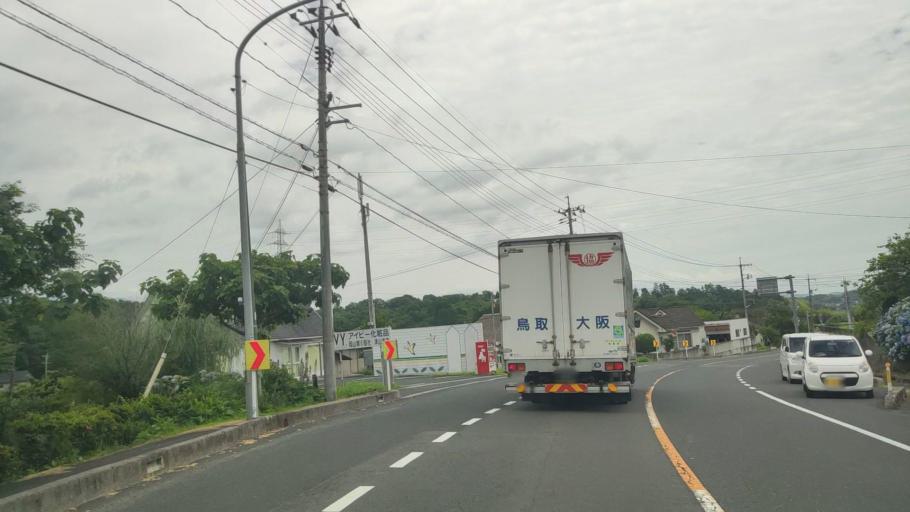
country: JP
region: Okayama
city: Tsuyama
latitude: 35.0766
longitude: 134.0852
